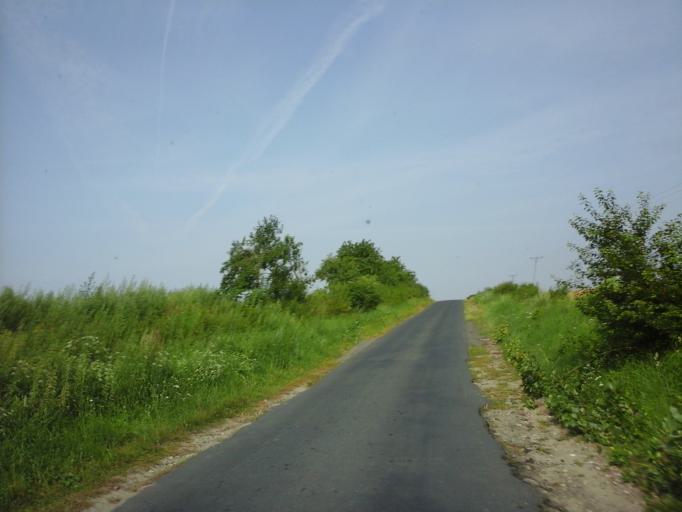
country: PL
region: West Pomeranian Voivodeship
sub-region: Powiat choszczenski
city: Pelczyce
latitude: 53.0479
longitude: 15.2936
